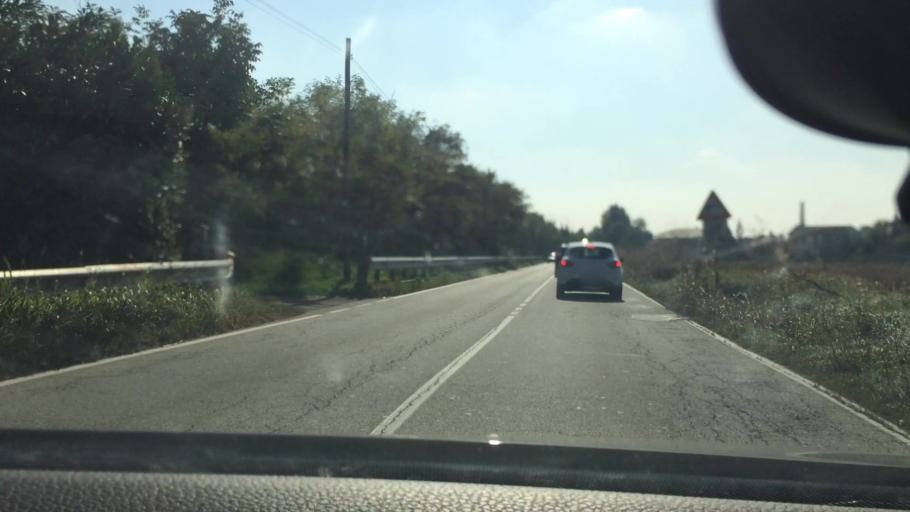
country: IT
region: Lombardy
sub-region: Citta metropolitana di Milano
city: Inveruno
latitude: 45.5225
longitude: 8.8595
